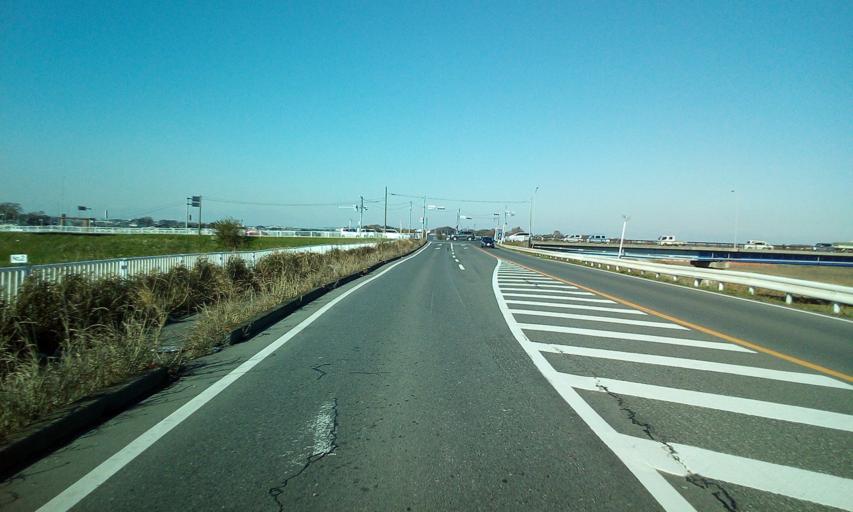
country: JP
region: Chiba
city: Noda
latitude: 35.9369
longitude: 139.8455
